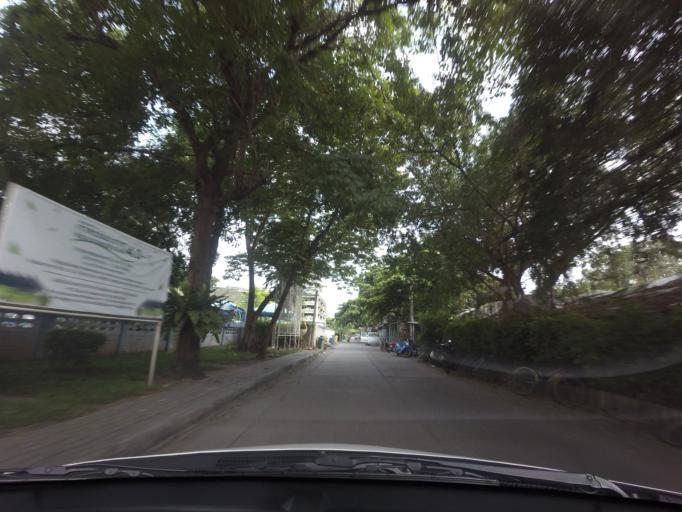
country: TH
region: Bangkok
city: Chatuchak
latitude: 13.8498
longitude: 100.5765
